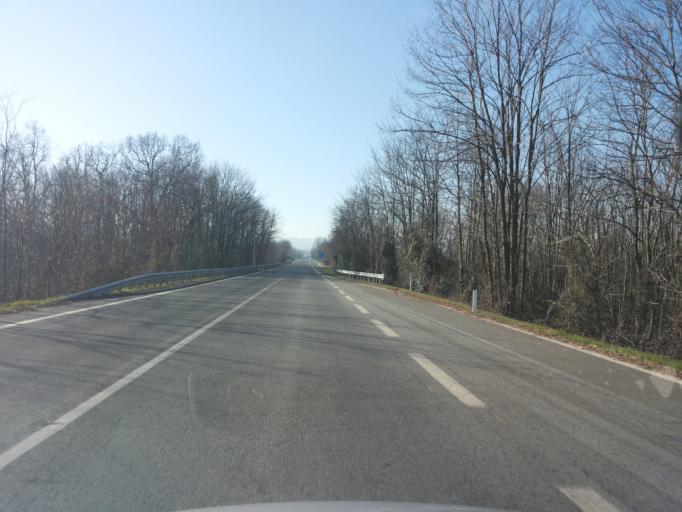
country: IT
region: Piedmont
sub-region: Provincia di Biella
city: Vergnasco
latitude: 45.4825
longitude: 8.0998
